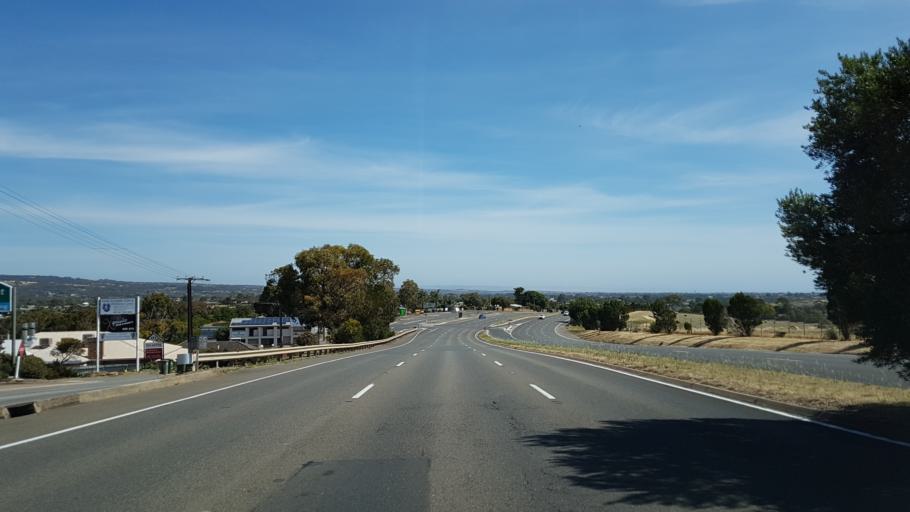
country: AU
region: South Australia
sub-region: Marion
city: Trott Park
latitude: -35.0688
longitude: 138.5547
